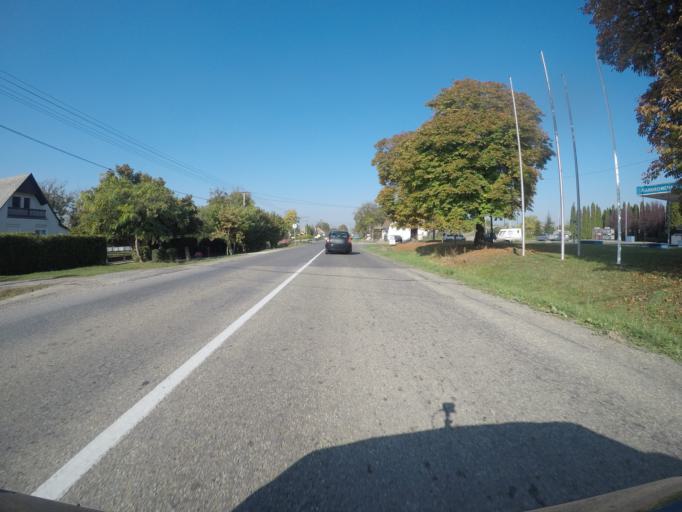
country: HU
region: Tolna
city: Szedres
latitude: 46.4701
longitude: 18.6859
